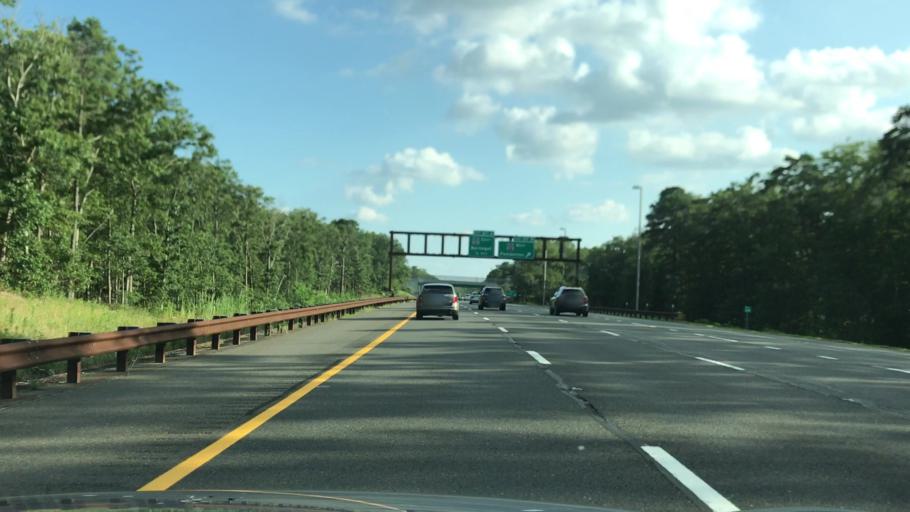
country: US
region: New Jersey
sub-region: Ocean County
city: Barnegat
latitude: 39.7626
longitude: -74.2505
